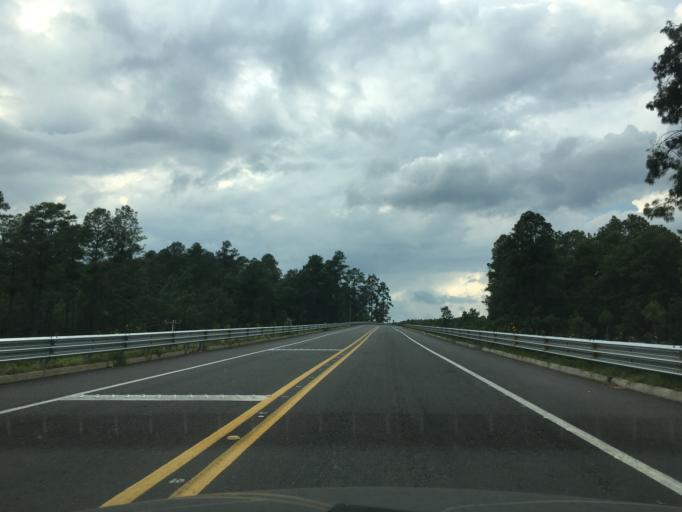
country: MX
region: Michoacan
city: Angahuan
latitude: 19.5164
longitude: -102.1739
